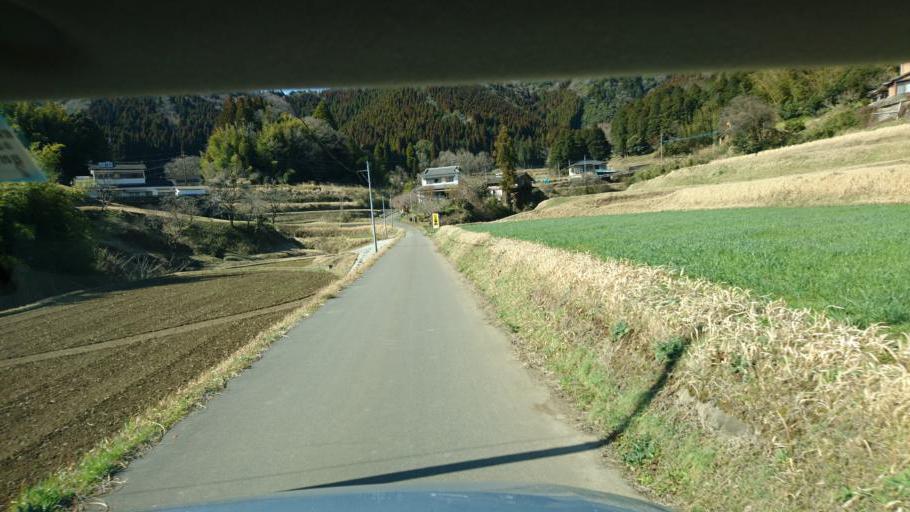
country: JP
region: Oita
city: Takedamachi
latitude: 32.7209
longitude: 131.3060
